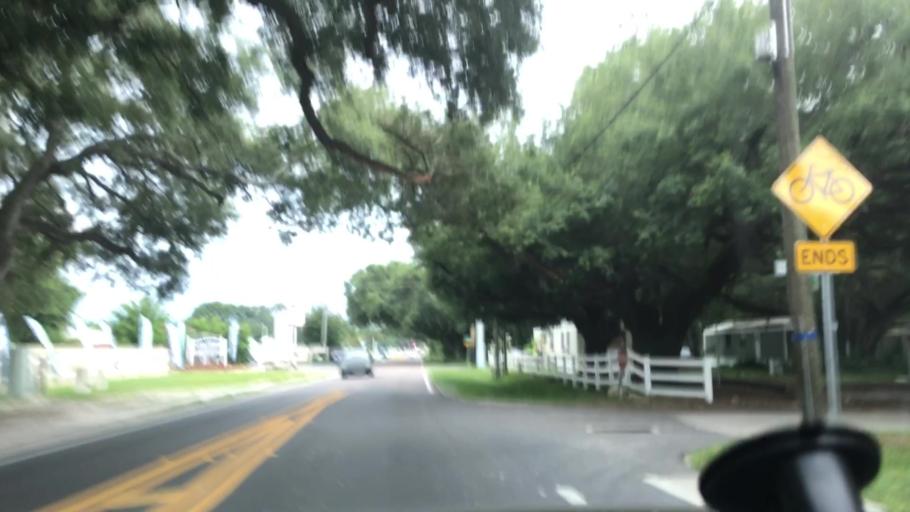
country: US
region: Florida
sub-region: Hillsborough County
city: Mango
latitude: 27.9859
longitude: -82.3188
